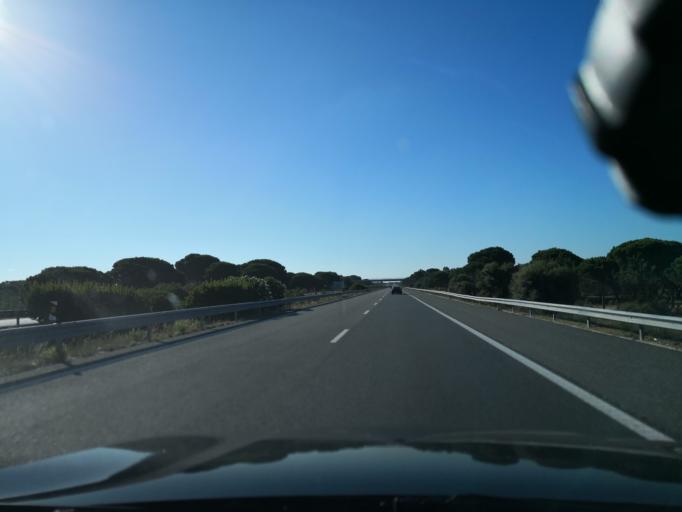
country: PT
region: Setubal
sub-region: Grandola
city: Grandola
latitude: 38.1564
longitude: -8.4765
